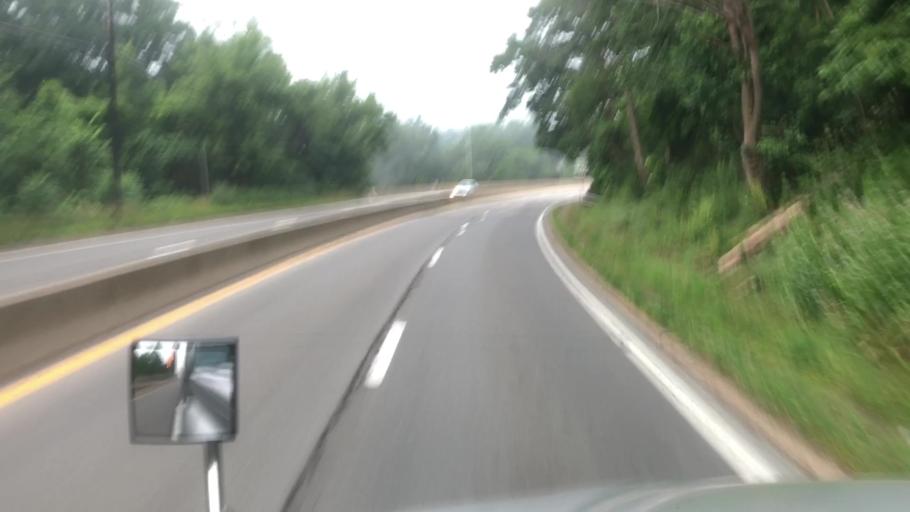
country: US
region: Pennsylvania
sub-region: Venango County
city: Franklin
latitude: 41.3958
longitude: -79.8211
